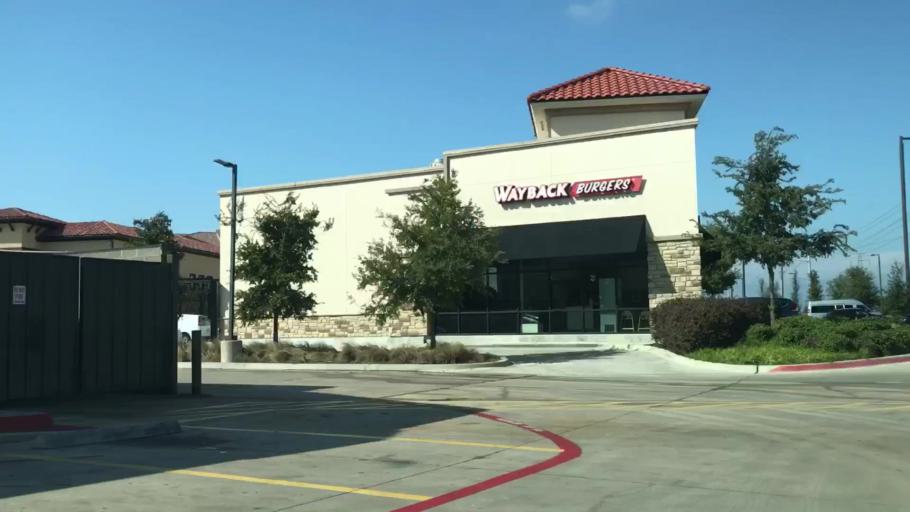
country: US
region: Texas
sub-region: Dallas County
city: Farmers Branch
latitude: 32.8963
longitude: -96.9391
